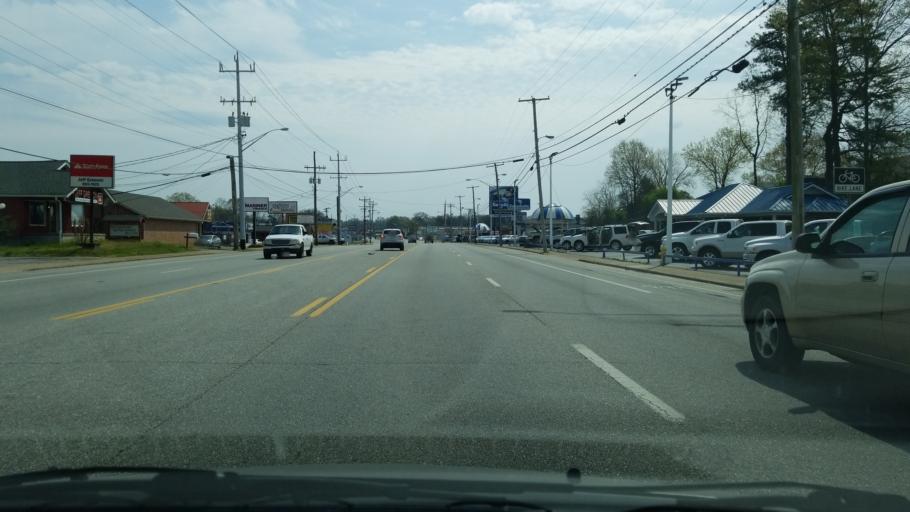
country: US
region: Tennessee
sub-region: Hamilton County
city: East Ridge
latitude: 34.9923
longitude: -85.2271
